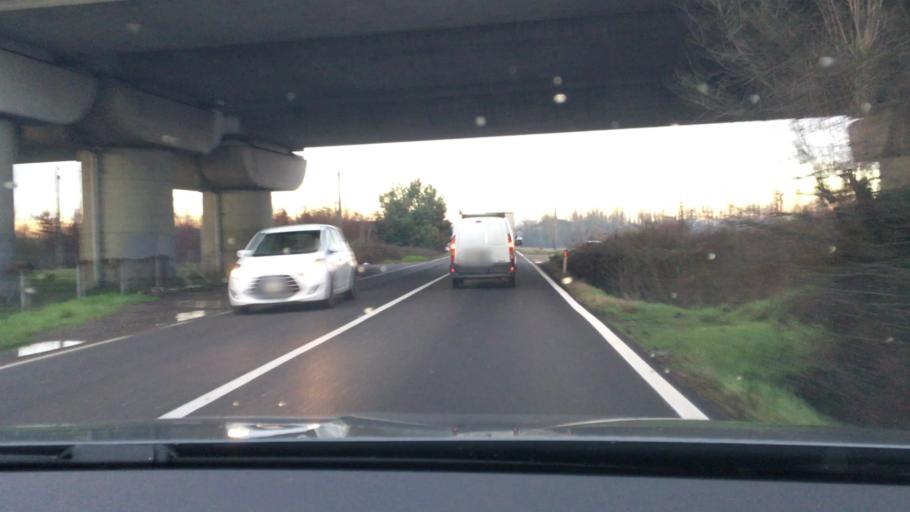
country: IT
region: Emilia-Romagna
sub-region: Provincia di Modena
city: Albareto
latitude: 44.6915
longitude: 10.9437
